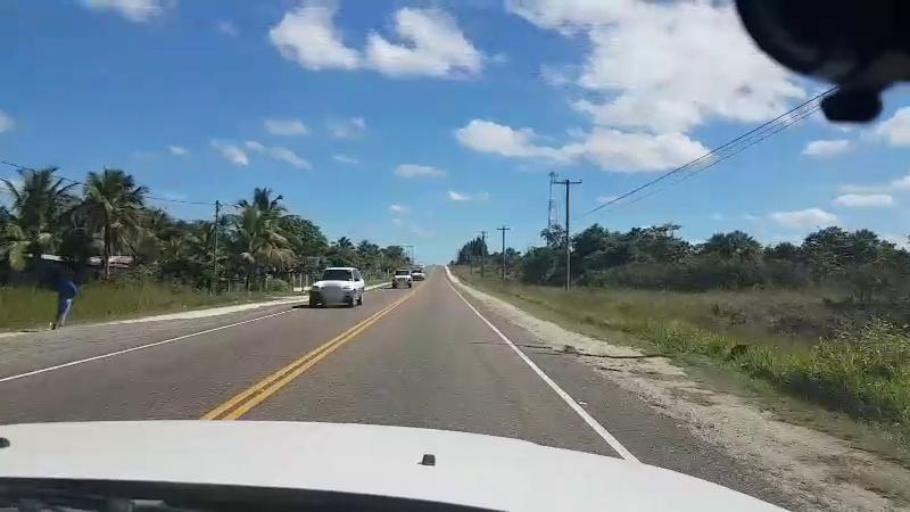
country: BZ
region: Cayo
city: Belmopan
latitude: 17.2770
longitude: -88.6642
